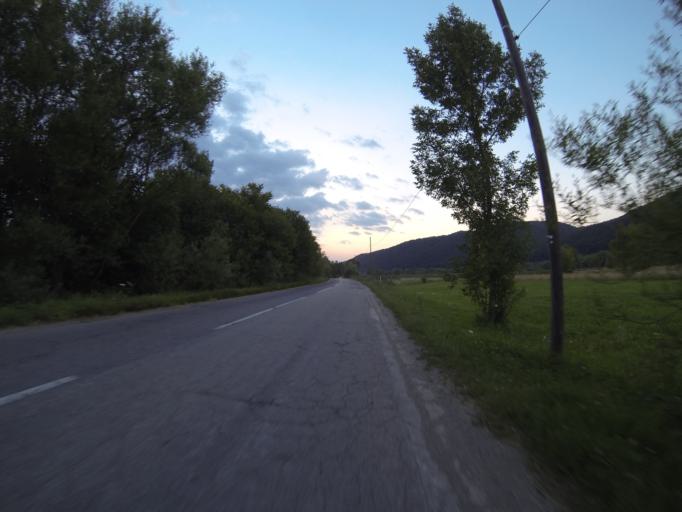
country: RO
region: Brasov
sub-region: Comuna Sinca Noua
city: Sinca Noua
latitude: 45.7307
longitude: 25.2341
